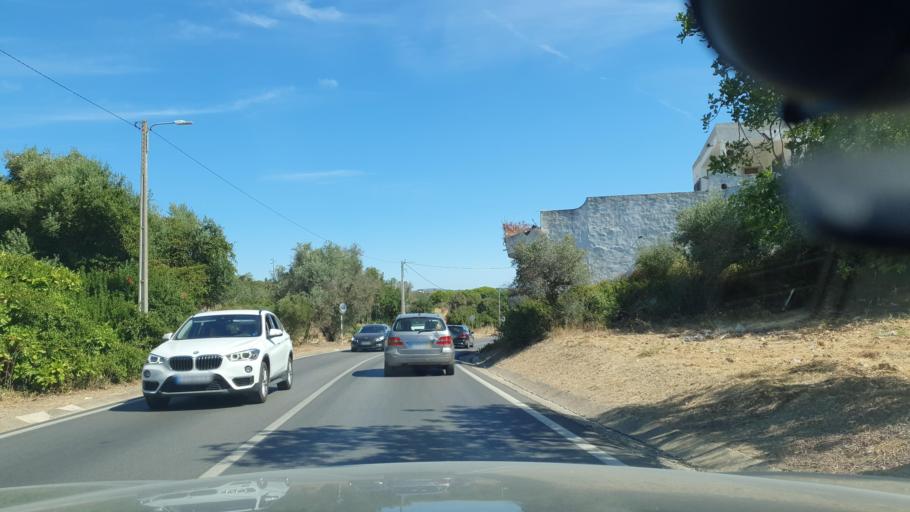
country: PT
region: Faro
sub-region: Albufeira
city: Guia
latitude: 37.1046
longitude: -8.3080
